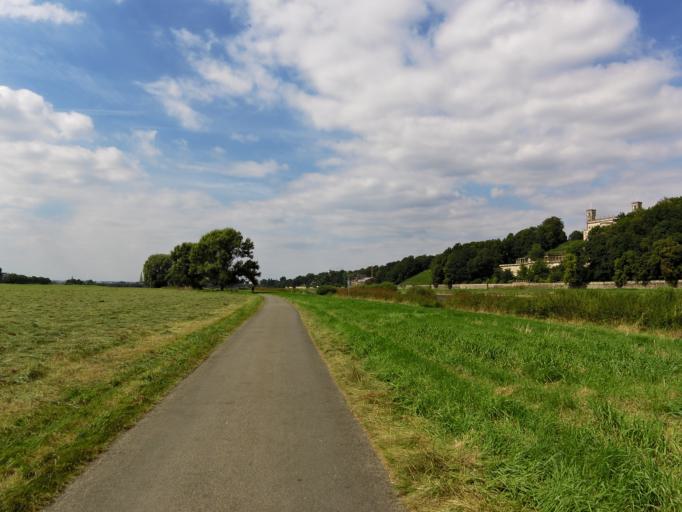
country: DE
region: Saxony
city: Albertstadt
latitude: 51.0612
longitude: 13.7977
